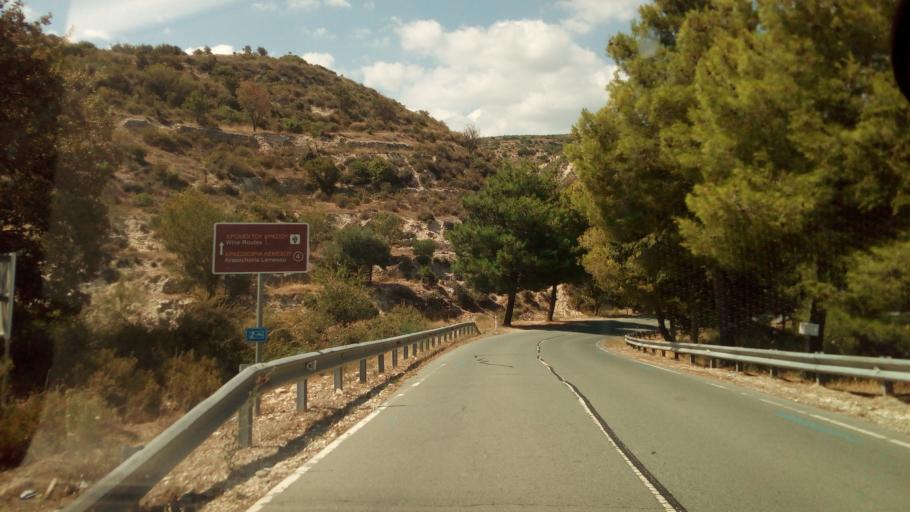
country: CY
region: Limassol
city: Pachna
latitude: 34.8321
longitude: 32.8507
